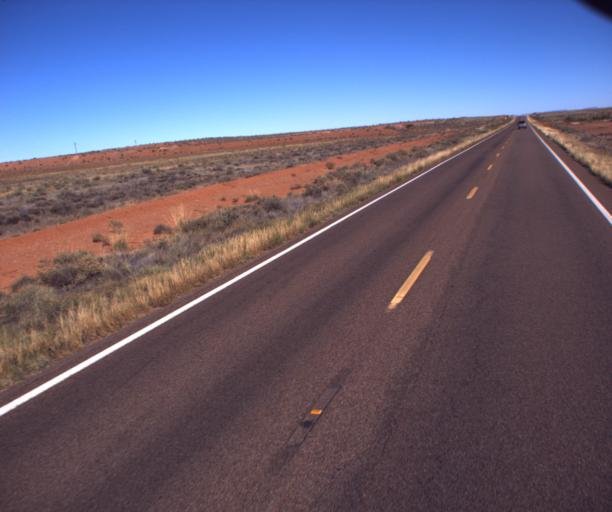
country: US
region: Arizona
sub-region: Navajo County
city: Holbrook
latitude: 34.8205
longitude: -110.1407
